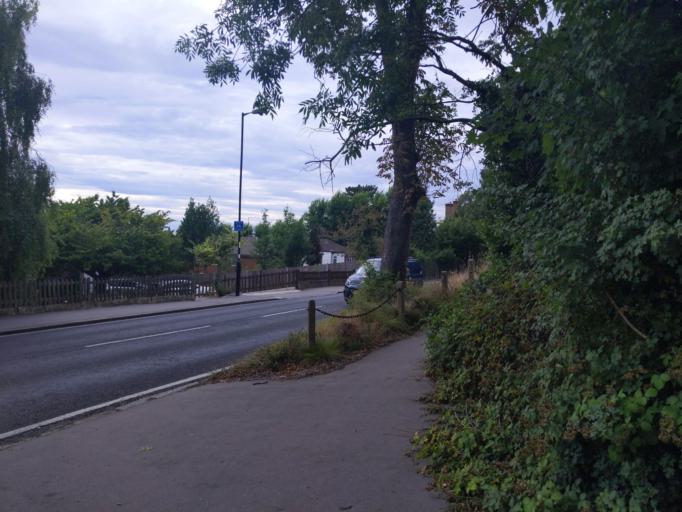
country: GB
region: England
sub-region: Greater London
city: South Croydon
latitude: 51.3531
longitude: -0.0876
